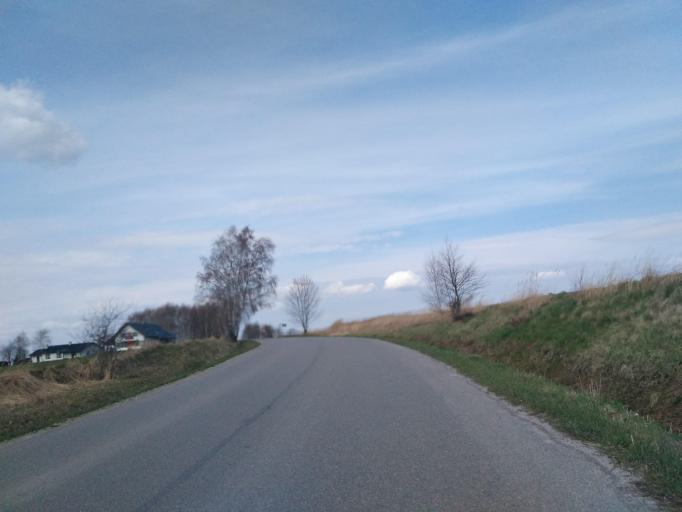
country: PL
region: Subcarpathian Voivodeship
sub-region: Powiat ropczycko-sedziszowski
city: Iwierzyce
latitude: 49.9998
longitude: 21.7986
